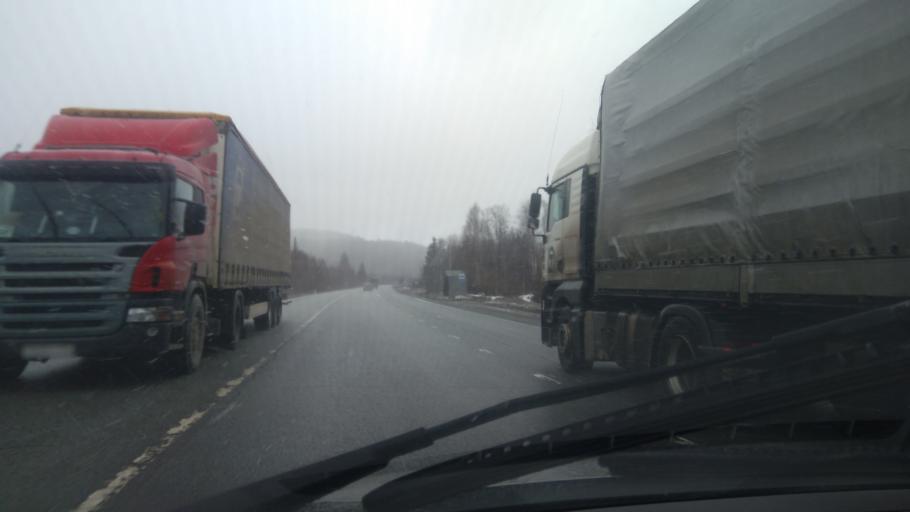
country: RU
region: Sverdlovsk
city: Arti
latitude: 56.7944
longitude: 58.6151
